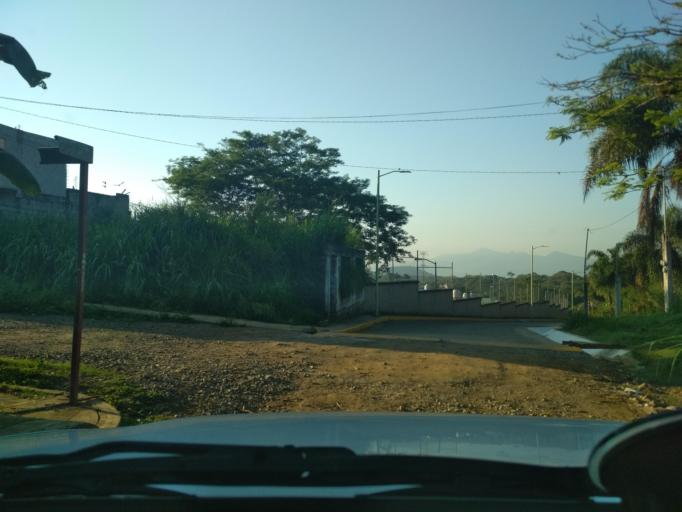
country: MX
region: Veracruz
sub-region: Fortin
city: Fraccionamiento Villas de la Llave
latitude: 18.9176
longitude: -96.9975
